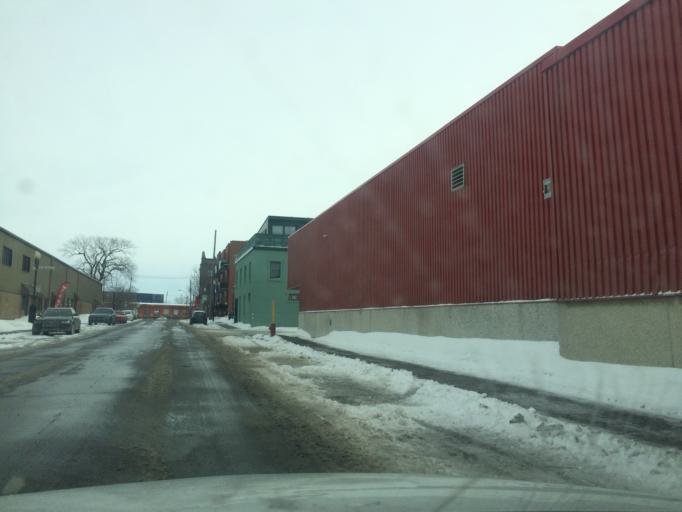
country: CA
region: Quebec
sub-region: Montreal
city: Montreal
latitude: 45.4861
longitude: -73.5597
